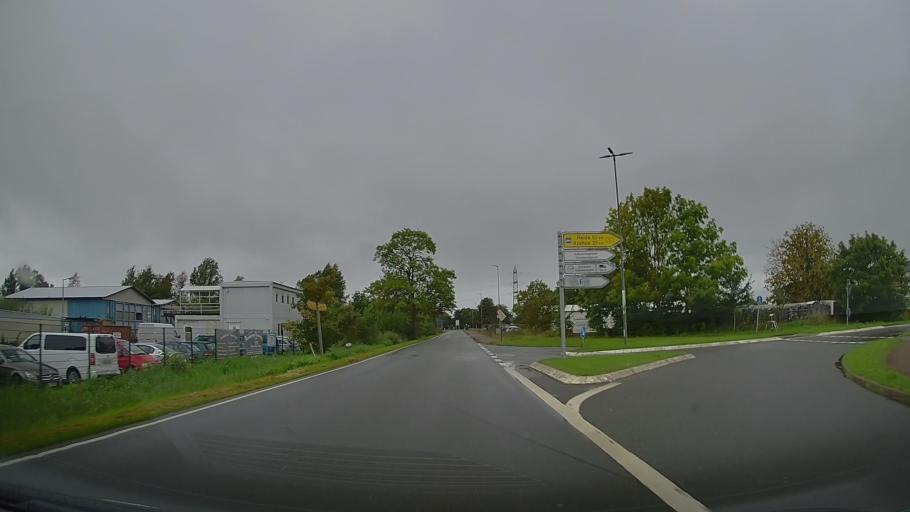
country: DE
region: Schleswig-Holstein
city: Buttel
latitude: 53.8990
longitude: 9.2319
